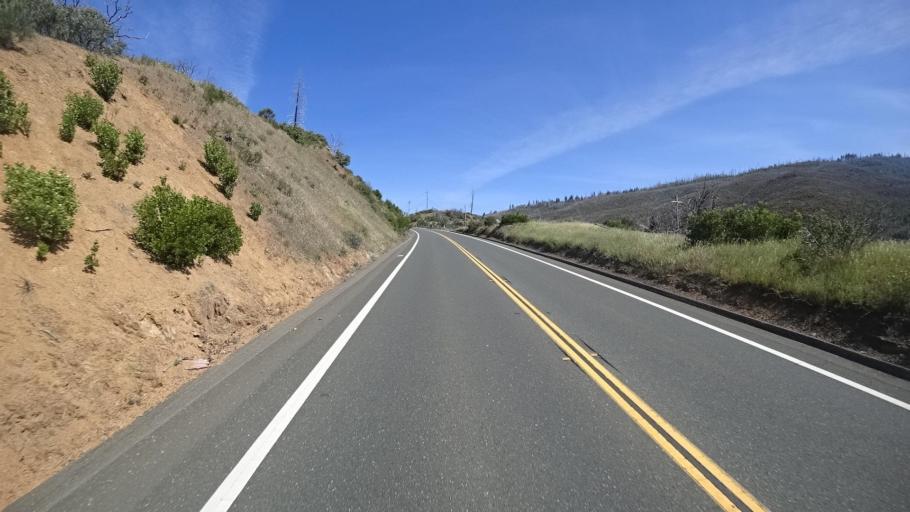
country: US
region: California
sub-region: Lake County
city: Cobb
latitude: 38.7964
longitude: -122.7038
